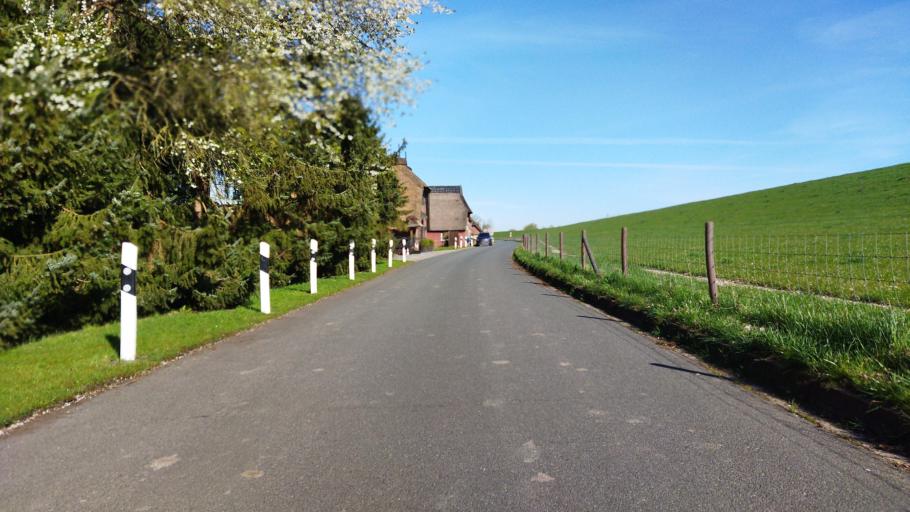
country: DE
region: Lower Saxony
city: Elsfleth
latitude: 53.2082
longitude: 8.4853
